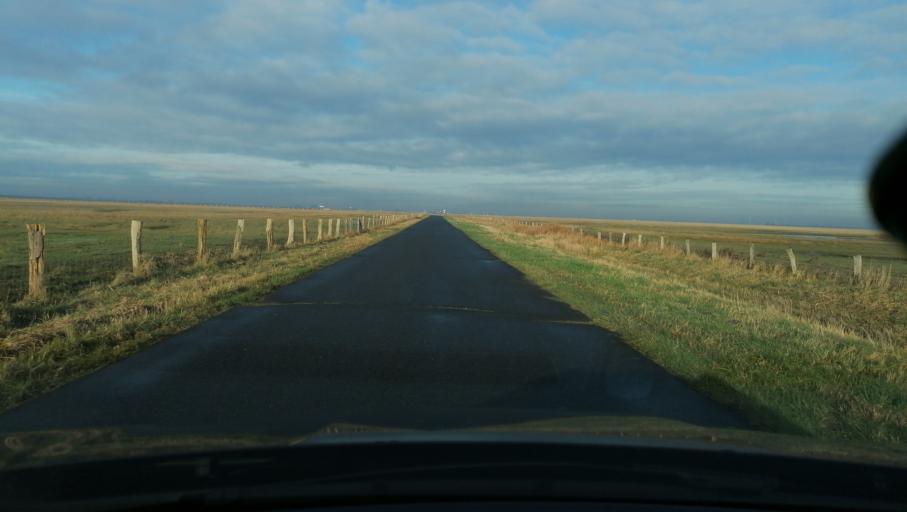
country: DE
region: Schleswig-Holstein
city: Friedrichsgabekoog
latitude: 54.1085
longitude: 8.9530
